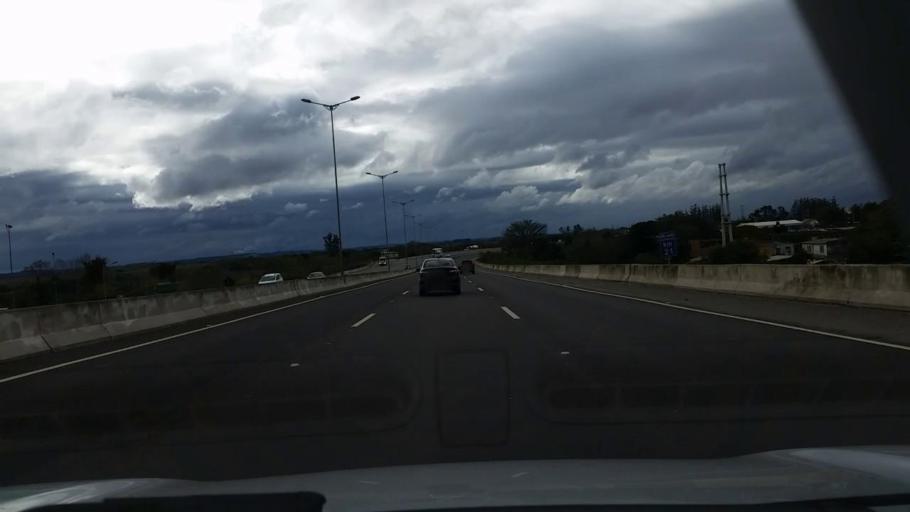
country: BR
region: Rio Grande do Sul
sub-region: Canoas
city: Canoas
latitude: -29.9665
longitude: -51.2018
